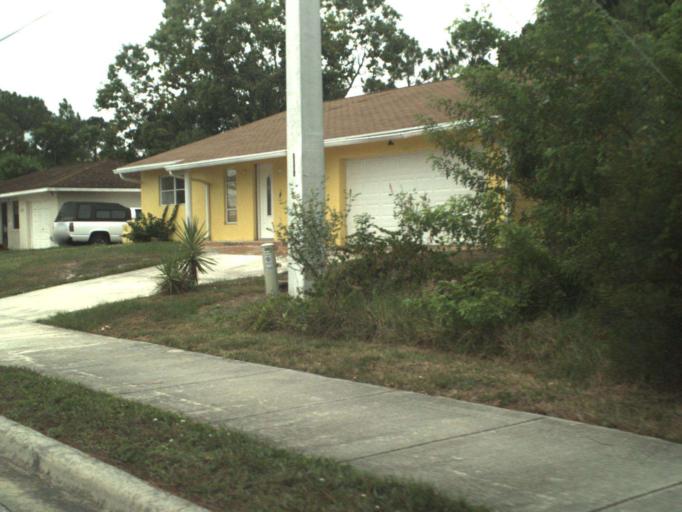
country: US
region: Florida
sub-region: Saint Lucie County
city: Port Saint Lucie
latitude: 27.2919
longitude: -80.3487
